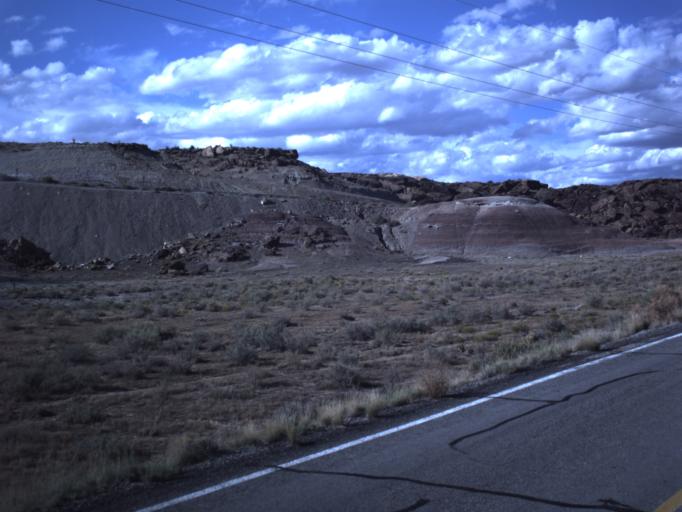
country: US
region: Utah
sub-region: San Juan County
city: Blanding
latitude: 37.3251
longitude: -109.3199
